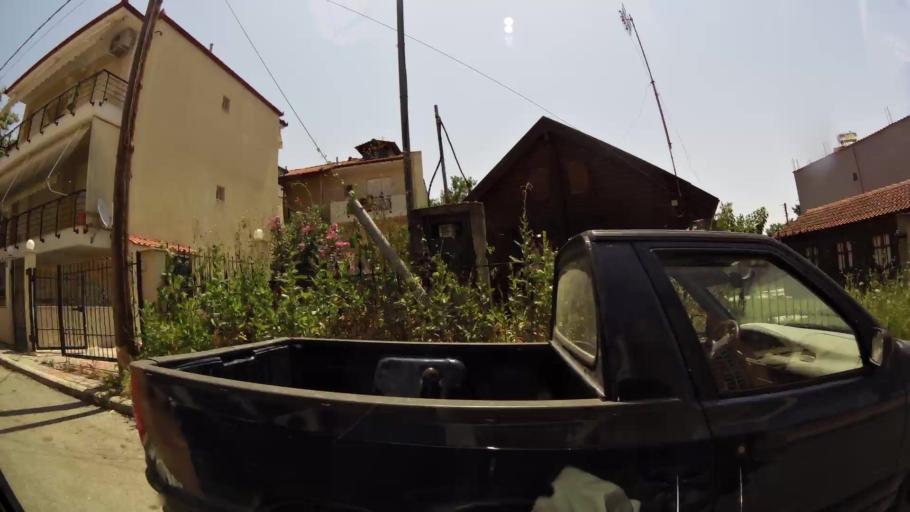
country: GR
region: Central Macedonia
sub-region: Nomos Thessalonikis
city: Nea Michaniona
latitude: 40.4764
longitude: 22.8673
